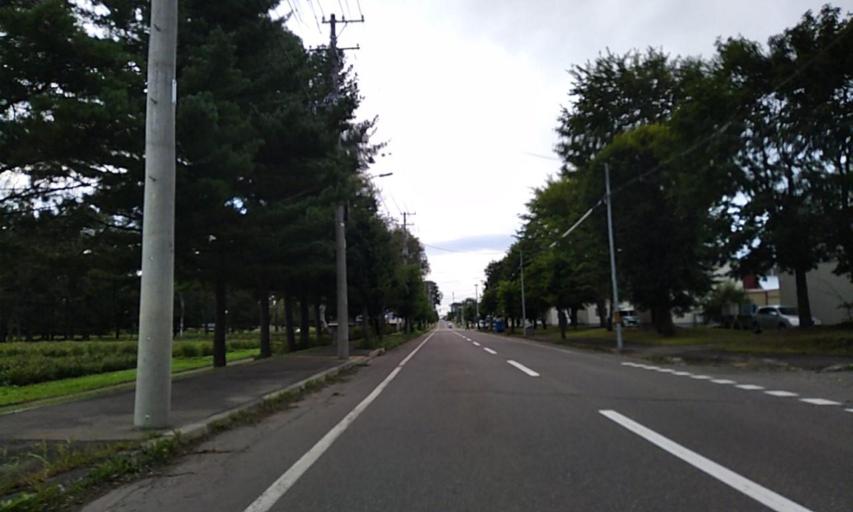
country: JP
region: Hokkaido
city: Obihiro
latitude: 42.9200
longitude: 143.0418
